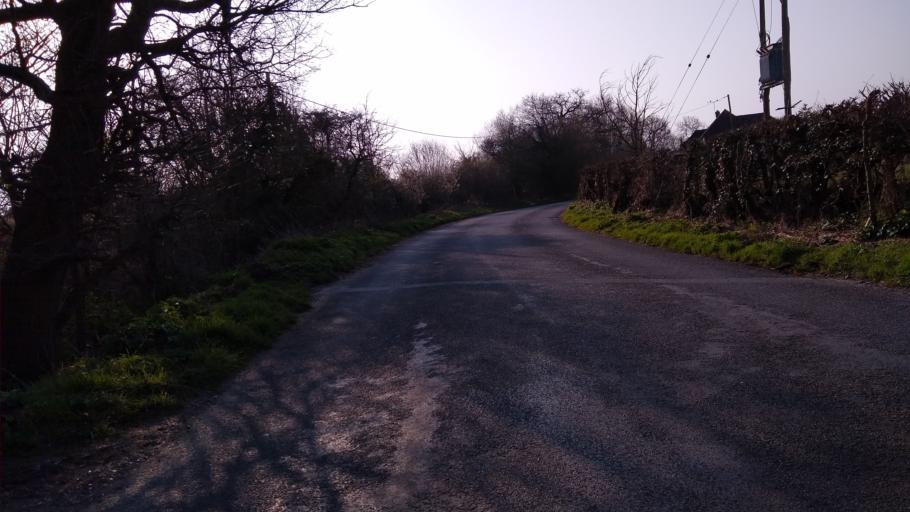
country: GB
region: England
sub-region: Wokingham
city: Winnersh
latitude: 51.4402
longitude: -0.8622
